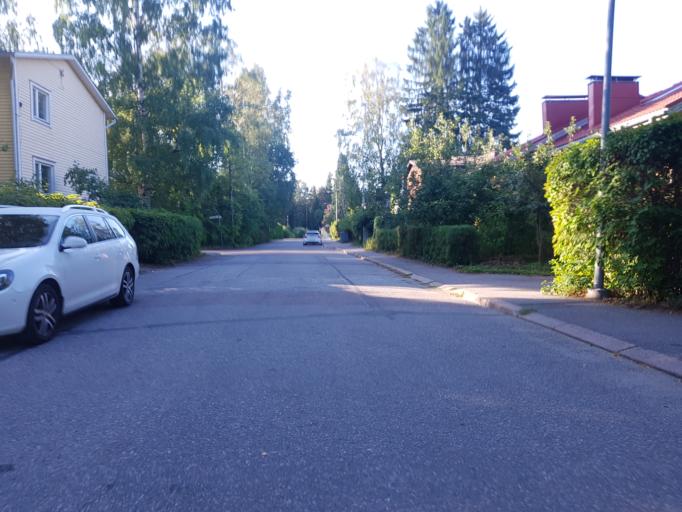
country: FI
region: Uusimaa
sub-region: Helsinki
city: Helsinki
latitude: 60.2426
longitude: 24.9191
